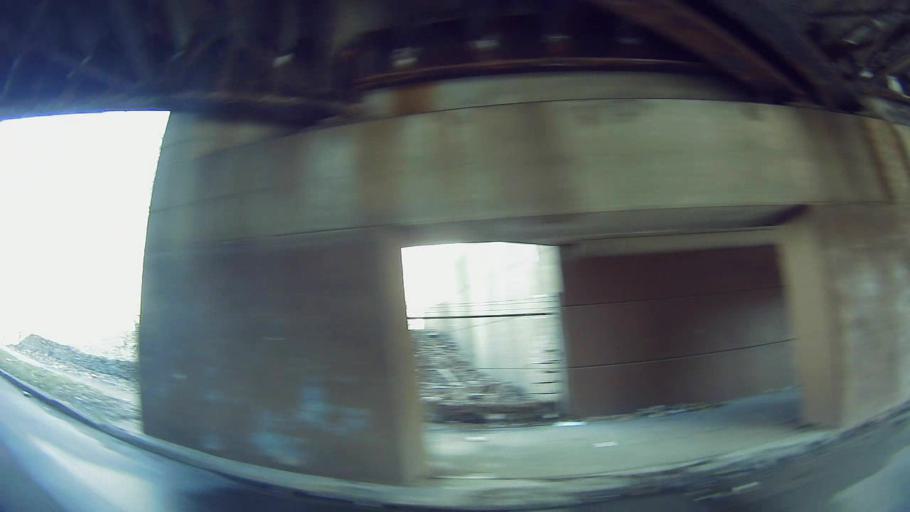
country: US
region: Michigan
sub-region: Oakland County
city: Hazel Park
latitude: 42.4340
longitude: -83.1024
